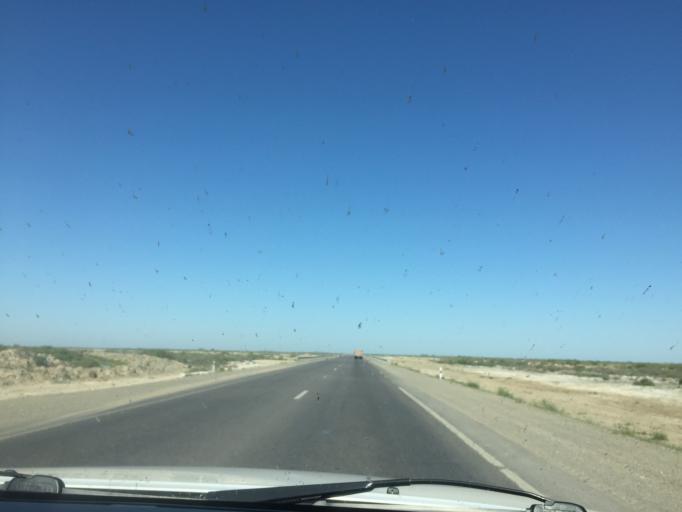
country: KZ
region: Qyzylorda
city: Terenozek
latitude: 44.8856
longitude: 65.1951
